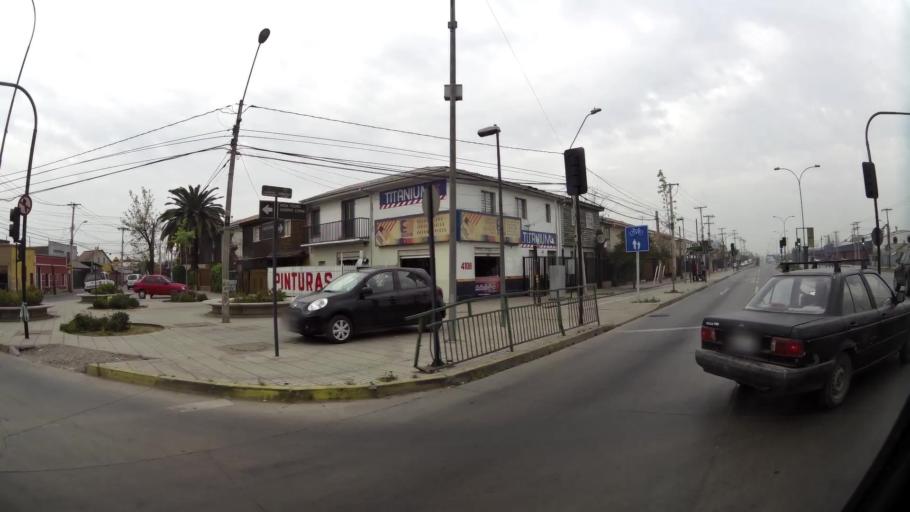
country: CL
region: Santiago Metropolitan
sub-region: Provincia de Santiago
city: Santiago
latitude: -33.4782
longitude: -70.6908
